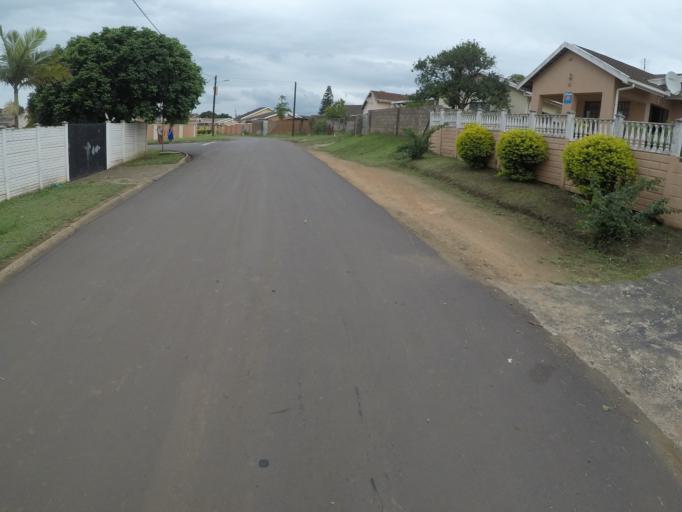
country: ZA
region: KwaZulu-Natal
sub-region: uThungulu District Municipality
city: Empangeni
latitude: -28.7736
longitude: 31.8498
